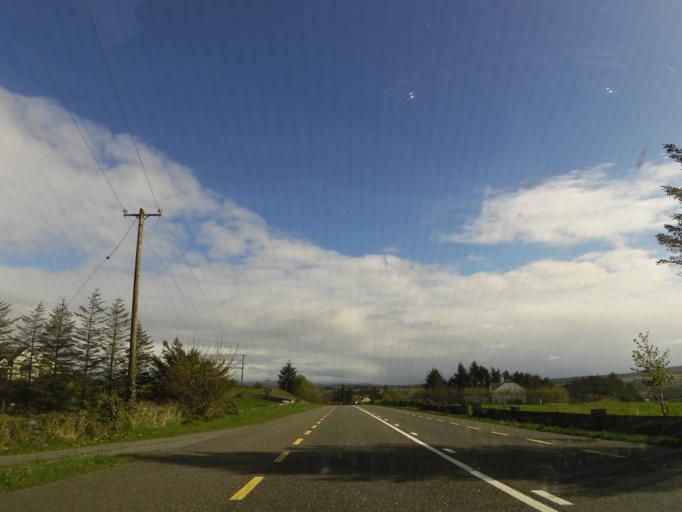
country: IE
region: Connaught
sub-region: Sligo
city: Tobercurry
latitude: 53.9197
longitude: -8.7873
